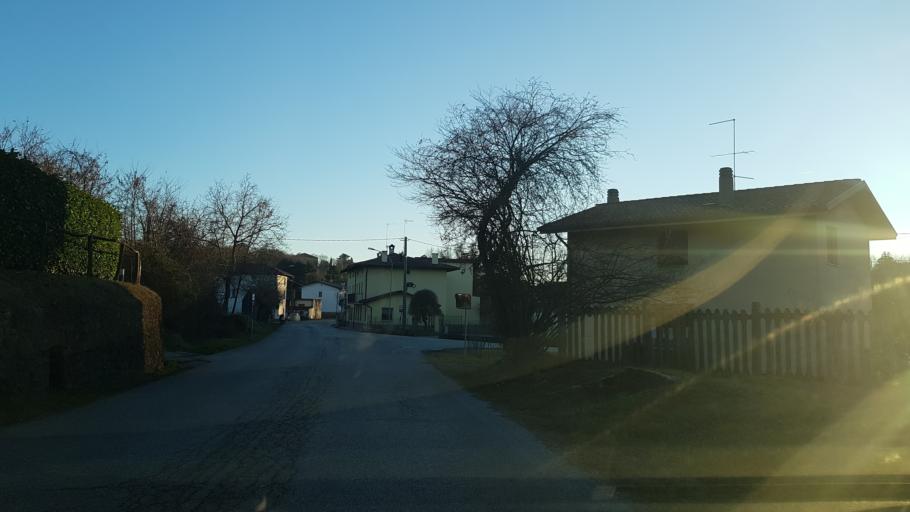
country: IT
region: Friuli Venezia Giulia
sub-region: Provincia di Udine
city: Tricesimo
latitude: 46.1733
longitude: 13.2175
